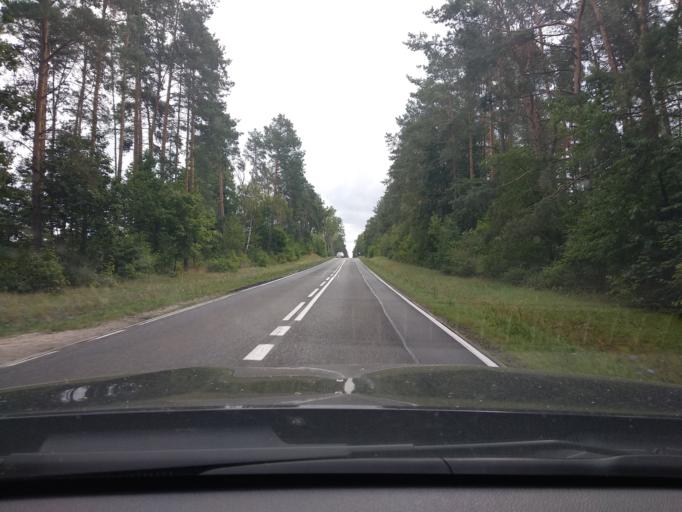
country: PL
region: Masovian Voivodeship
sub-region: Powiat pultuski
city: Obryte
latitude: 52.6432
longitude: 21.2661
